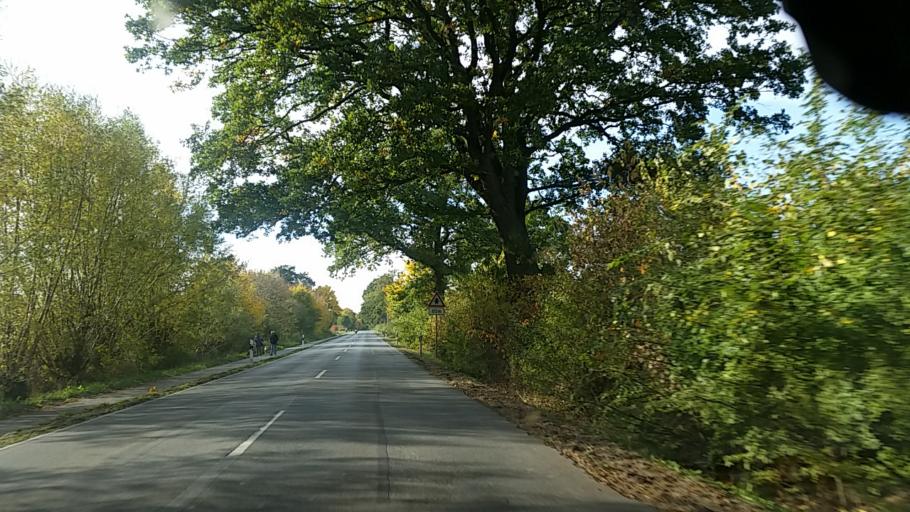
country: DE
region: Schleswig-Holstein
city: Jersbek
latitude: 53.7359
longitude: 10.2417
